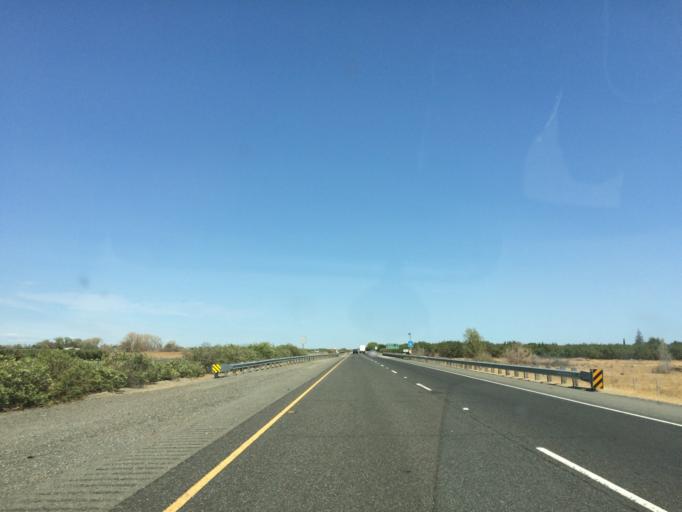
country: US
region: California
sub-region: Glenn County
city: Willows
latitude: 39.6328
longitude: -122.2041
